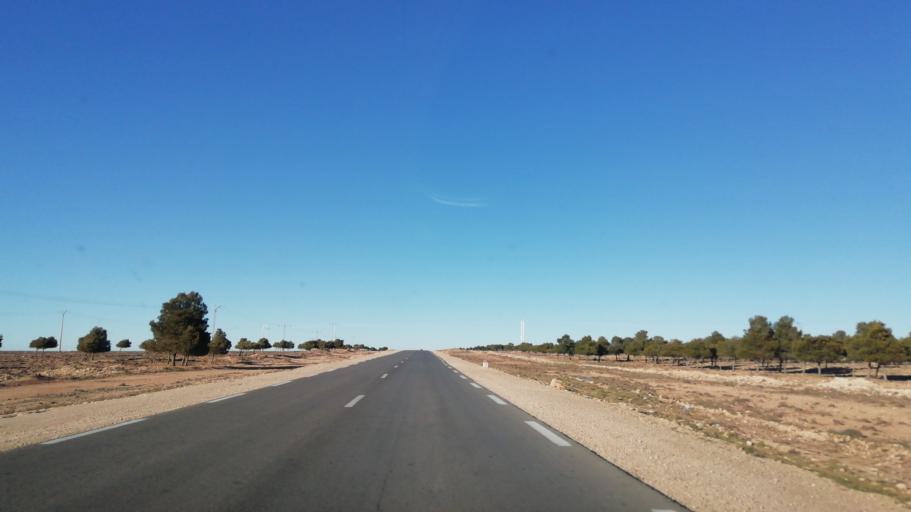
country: DZ
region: Tlemcen
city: Sebdou
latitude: 34.2414
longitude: -1.2569
